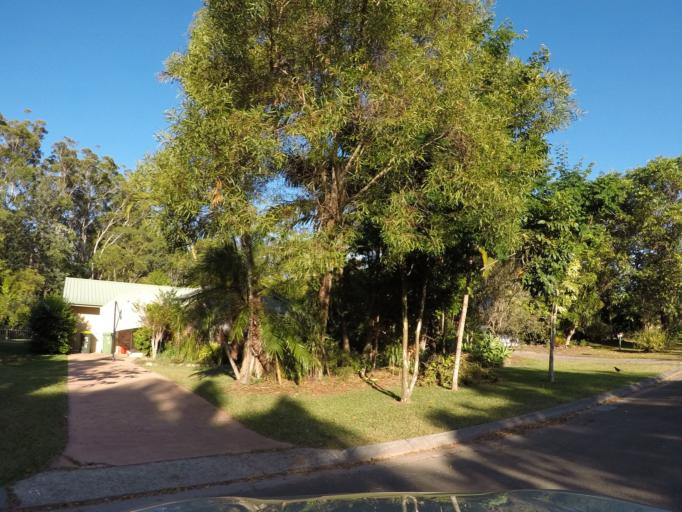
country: AU
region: Queensland
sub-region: Sunshine Coast
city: Nambour
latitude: -26.6200
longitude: 152.8603
